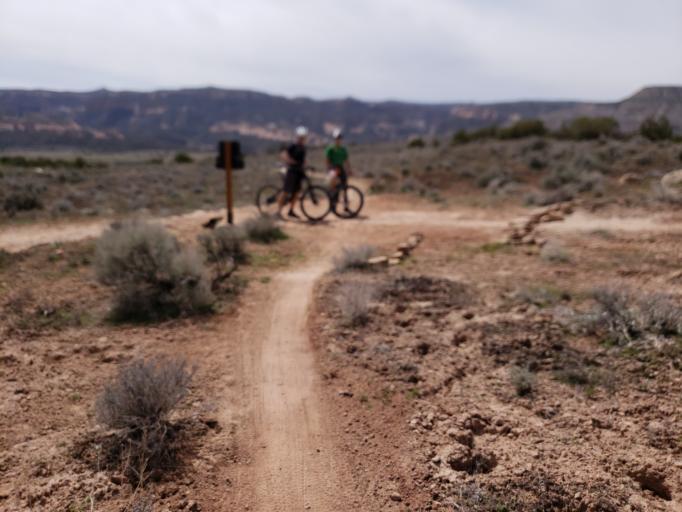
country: US
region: Colorado
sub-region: Mesa County
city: Loma
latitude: 39.1802
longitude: -108.8540
